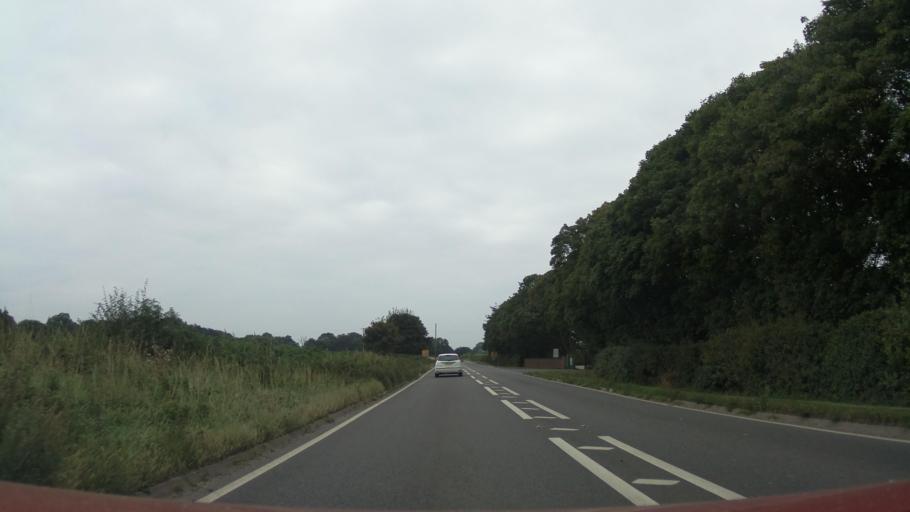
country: GB
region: England
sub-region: Shropshire
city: Shawbury
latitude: 52.8085
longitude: -2.6171
